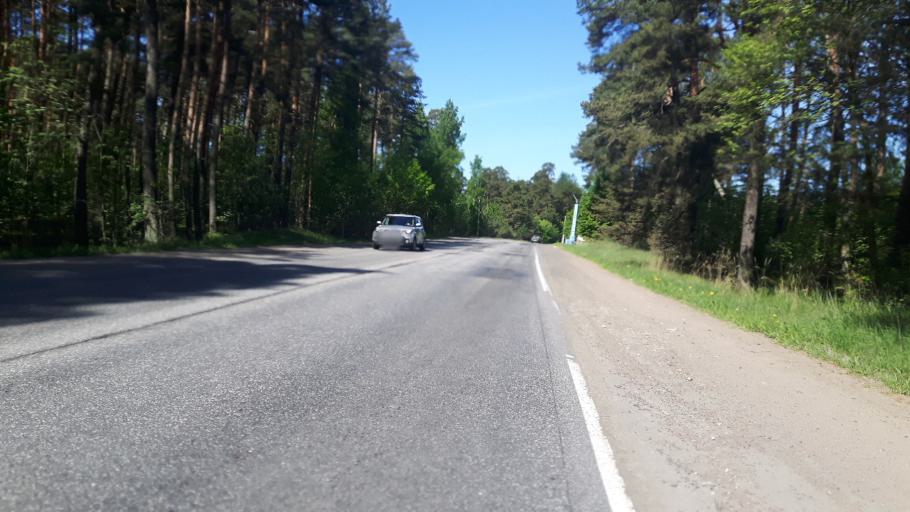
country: RU
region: Leningrad
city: Lebyazh'ye
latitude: 59.9586
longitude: 29.4410
